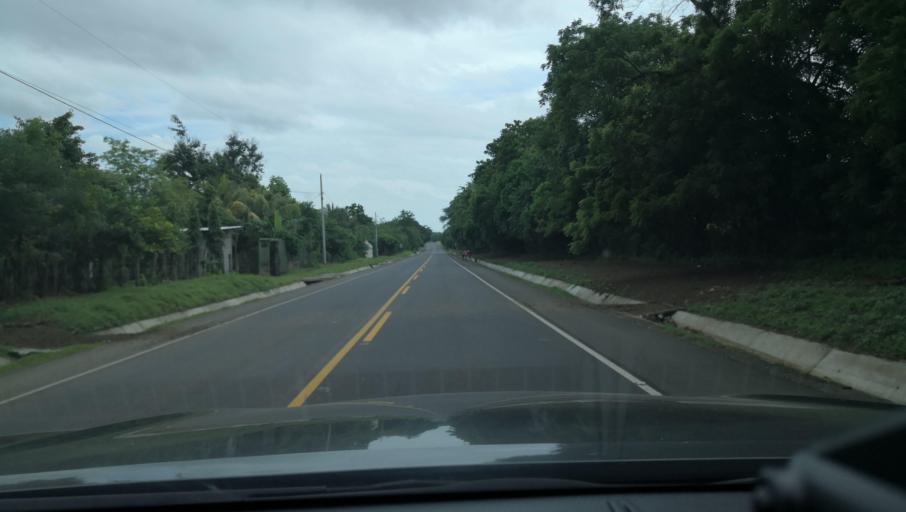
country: NI
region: Masaya
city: Nindiri
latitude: 12.0761
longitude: -86.1382
